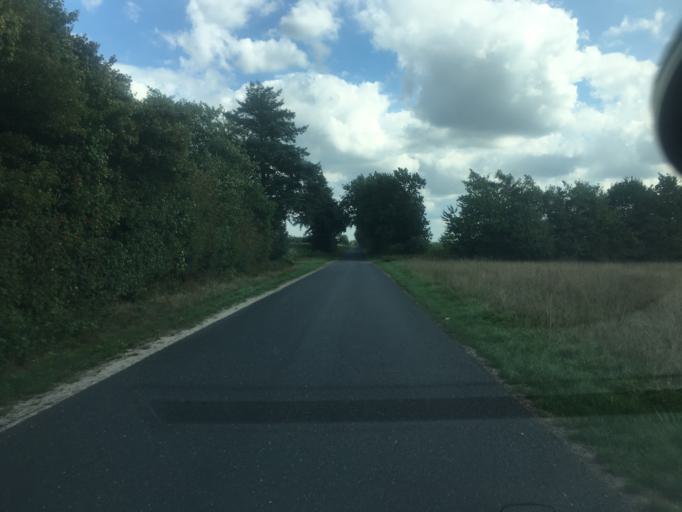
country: DK
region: South Denmark
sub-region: Tonder Kommune
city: Logumkloster
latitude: 55.0118
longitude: 9.0018
